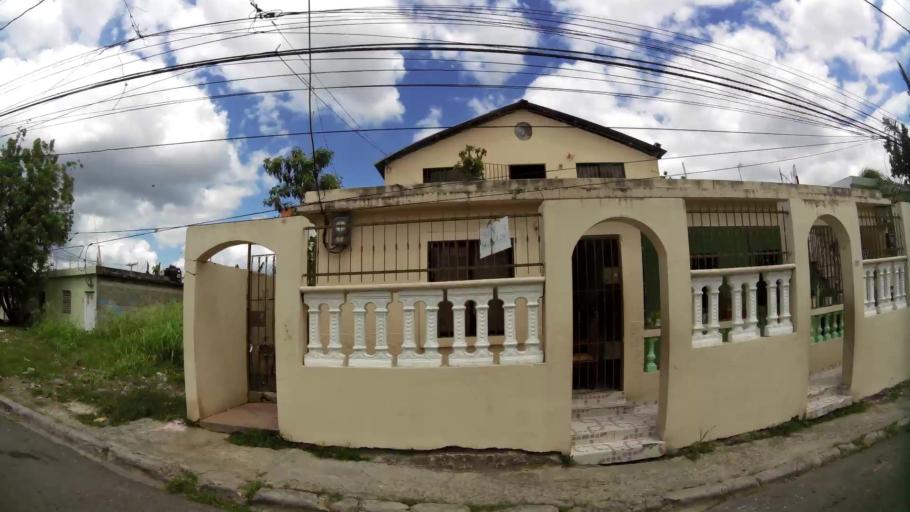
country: DO
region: Nacional
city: Ensanche Luperon
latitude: 18.5293
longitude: -69.9079
